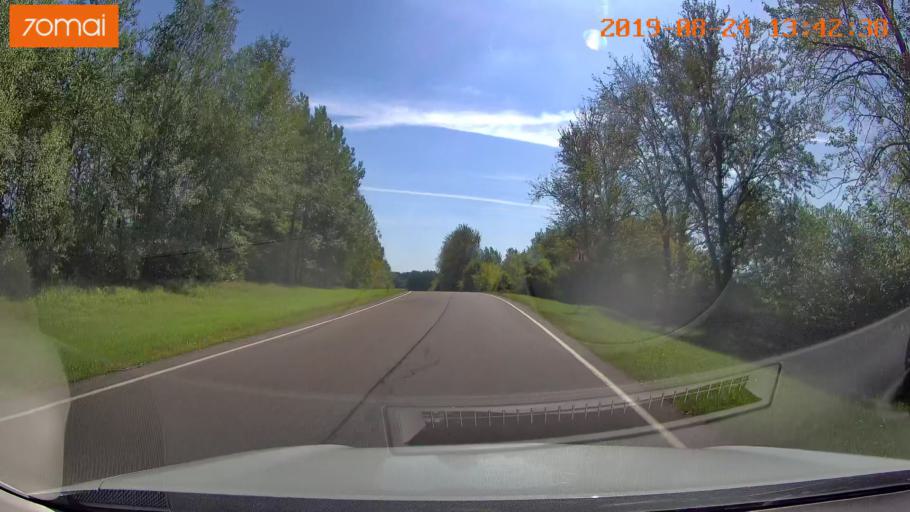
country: BY
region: Minsk
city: Samakhvalavichy
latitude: 53.7072
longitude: 27.5204
